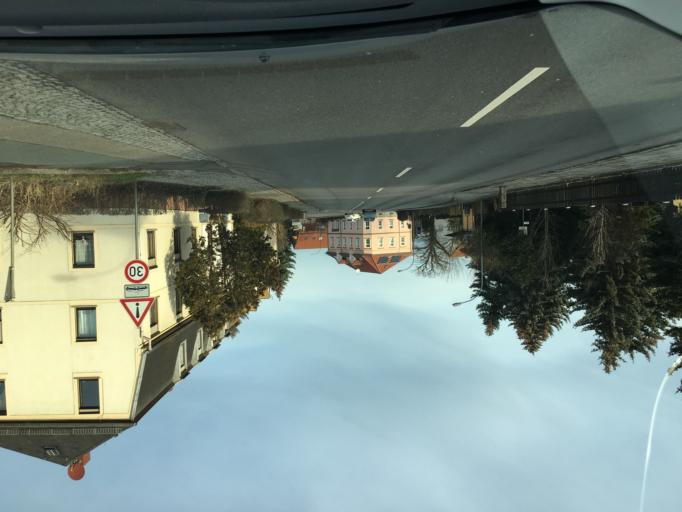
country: DE
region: Thuringia
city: Fockendorf
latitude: 51.0522
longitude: 12.4535
